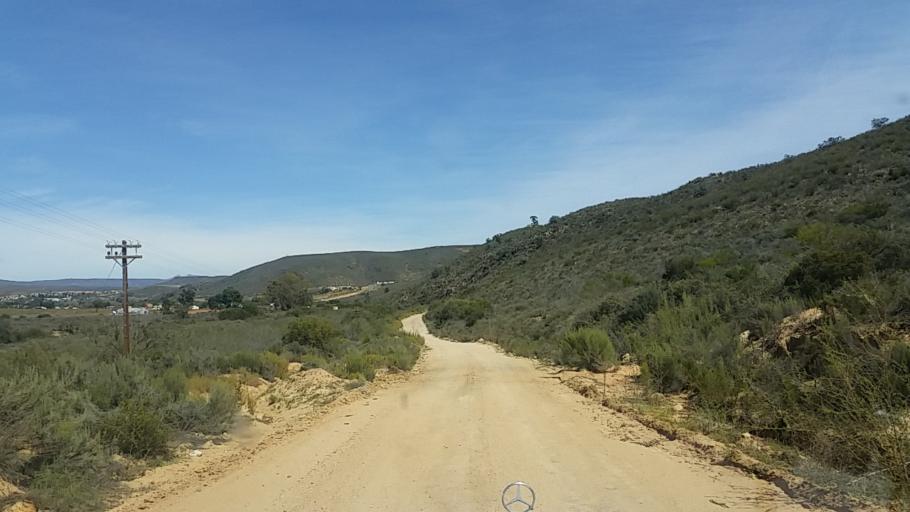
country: ZA
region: Western Cape
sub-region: Eden District Municipality
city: Knysna
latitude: -33.6387
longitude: 23.1494
